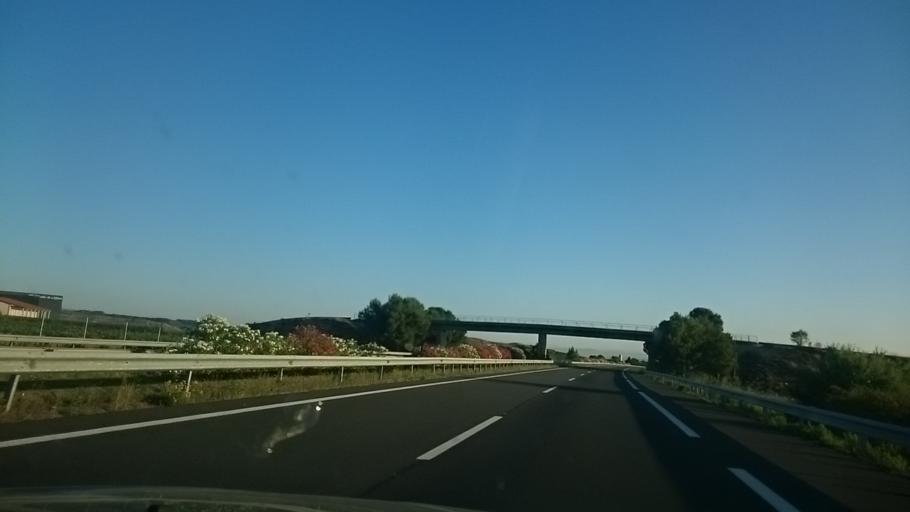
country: ES
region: La Rioja
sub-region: Provincia de La Rioja
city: Aldeanueva de Ebro
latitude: 42.2299
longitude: -1.9000
